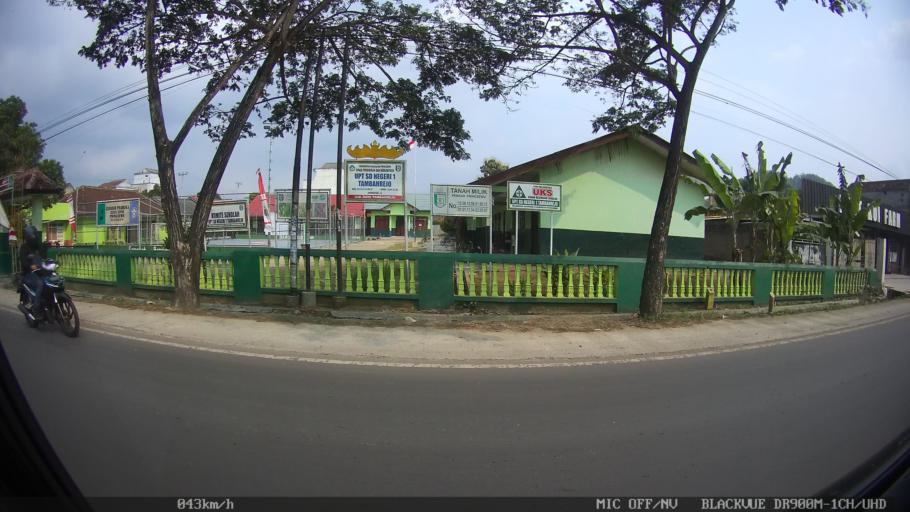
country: ID
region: Lampung
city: Gadingrejo
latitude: -5.3793
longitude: 105.0302
